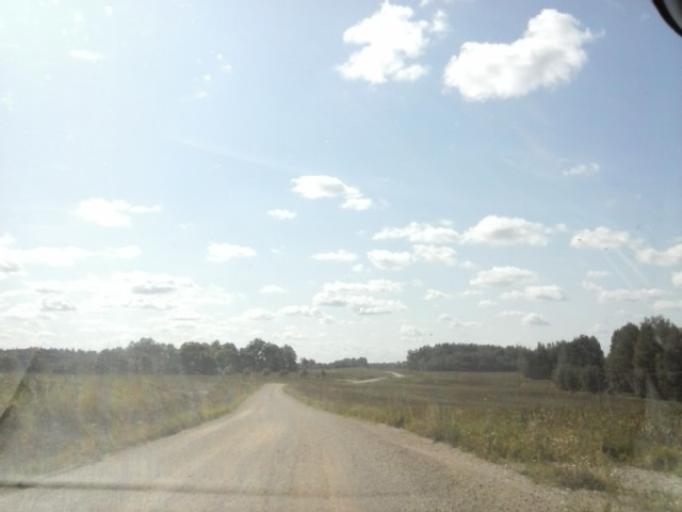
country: EE
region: Polvamaa
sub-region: Polva linn
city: Polva
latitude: 58.1084
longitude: 26.8634
